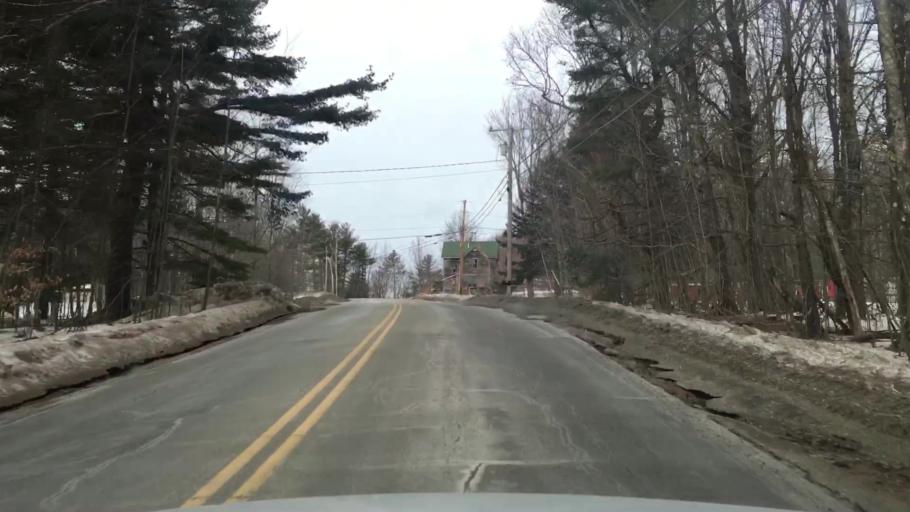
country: US
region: Maine
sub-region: Lincoln County
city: Whitefield
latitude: 44.2485
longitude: -69.6348
